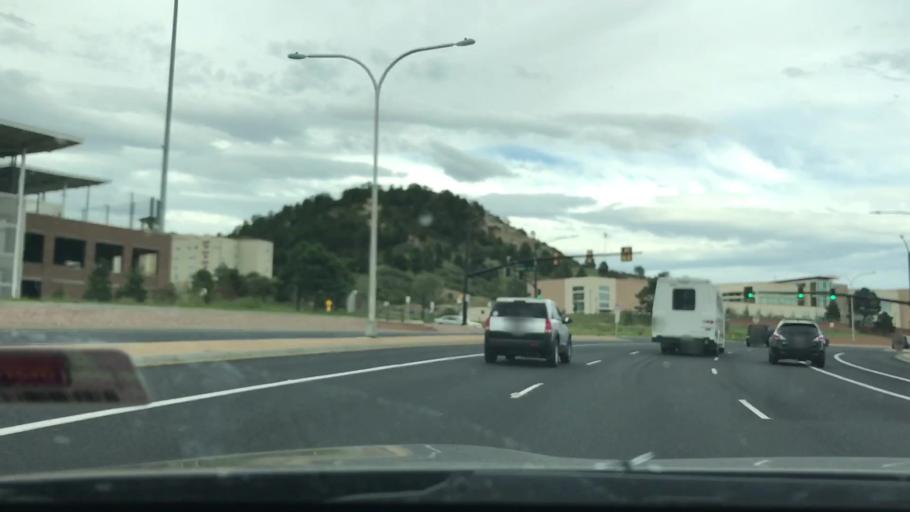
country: US
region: Colorado
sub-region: El Paso County
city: Colorado Springs
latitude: 38.8975
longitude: -104.8083
